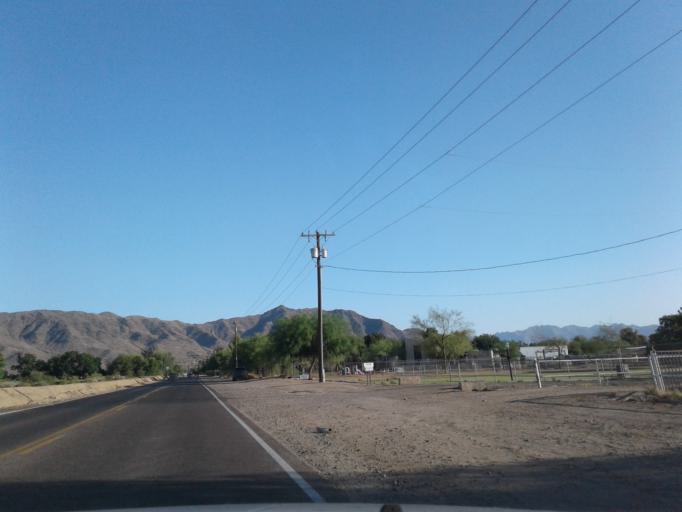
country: US
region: Arizona
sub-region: Maricopa County
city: Laveen
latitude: 33.3728
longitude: -112.1176
